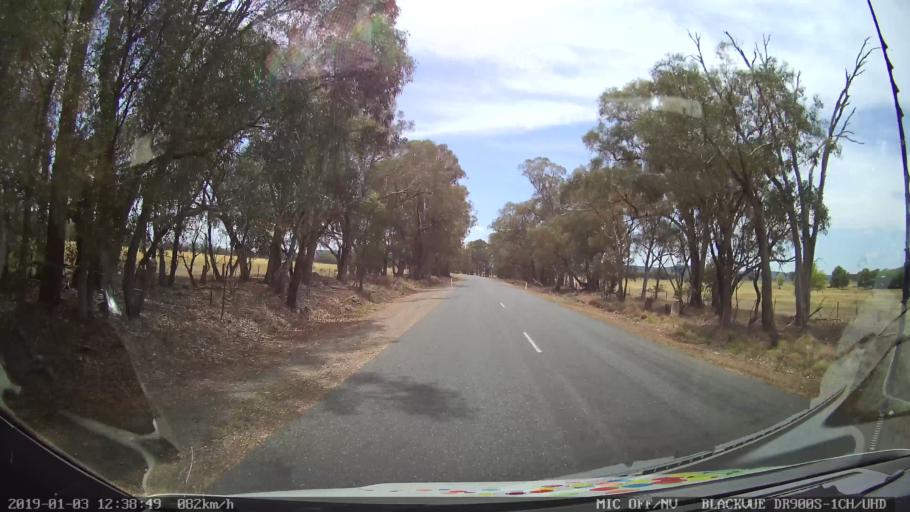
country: AU
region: New South Wales
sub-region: Weddin
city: Grenfell
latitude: -33.8304
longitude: 148.2002
